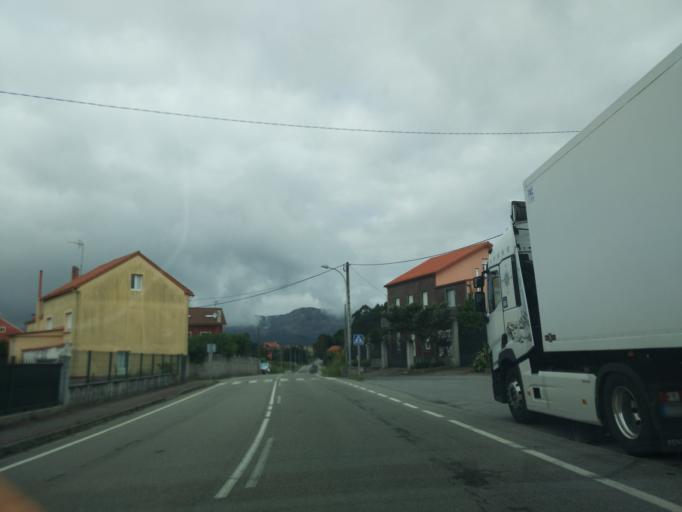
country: ES
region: Galicia
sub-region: Provincia da Coruna
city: Boiro
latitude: 42.6418
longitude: -8.8660
